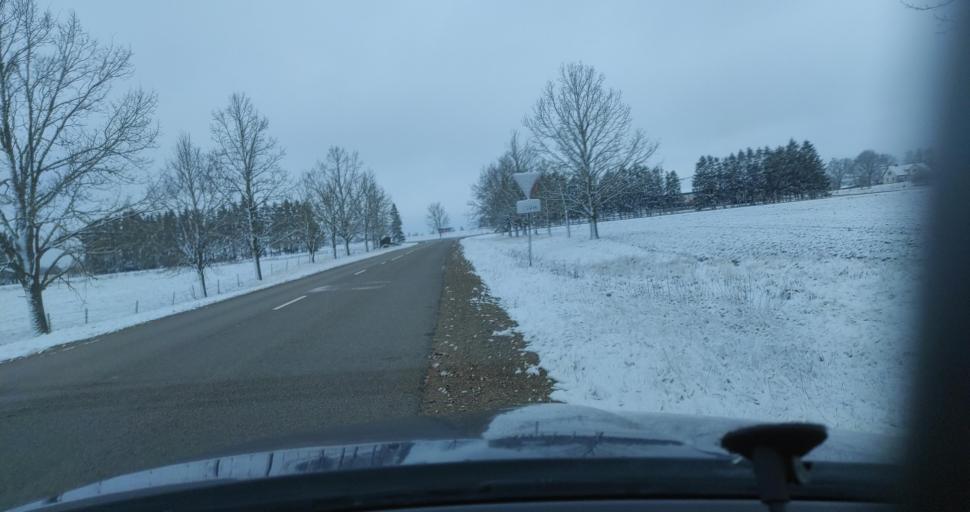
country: LV
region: Skrunda
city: Skrunda
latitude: 56.8469
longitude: 22.2263
